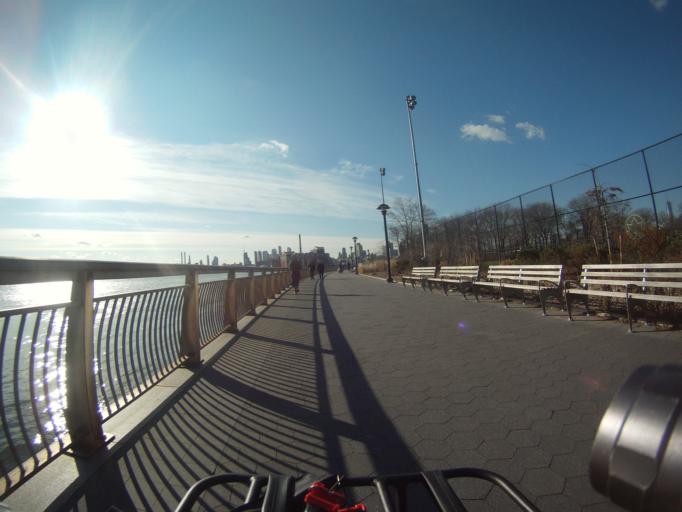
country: US
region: New York
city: New York City
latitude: 40.7121
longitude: -73.9765
